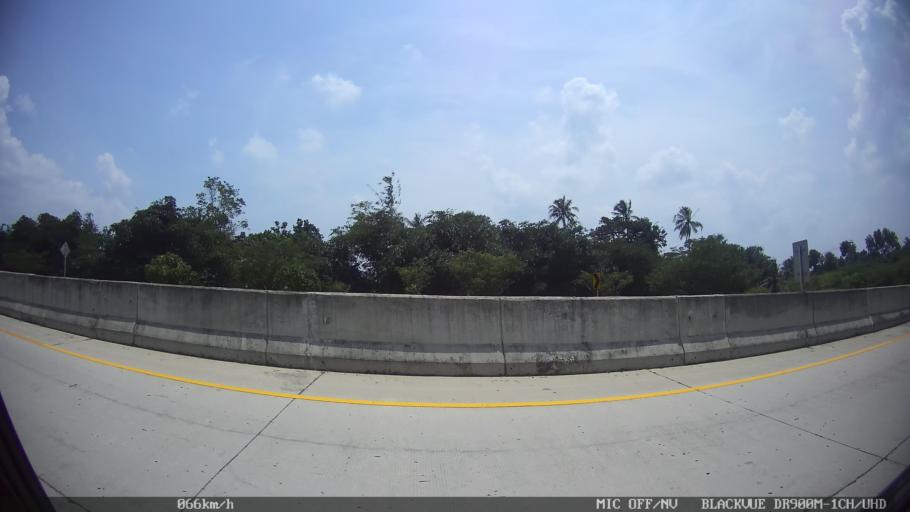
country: ID
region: Lampung
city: Natar
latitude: -5.2940
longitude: 105.2360
